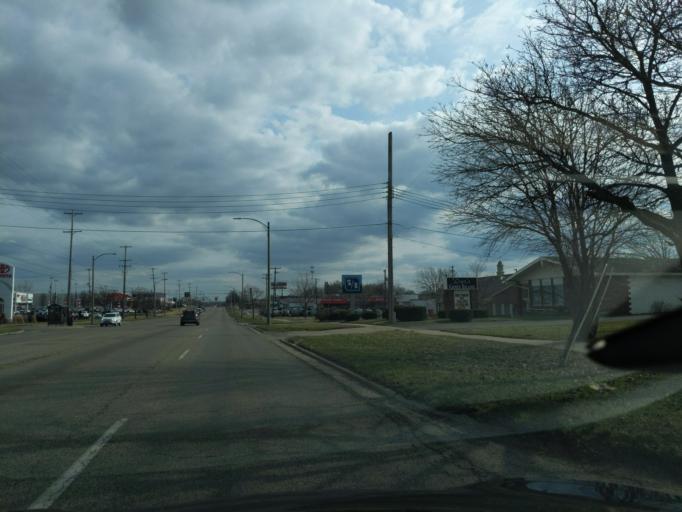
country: US
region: Michigan
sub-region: Ingham County
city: Holt
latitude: 42.6763
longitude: -84.5382
